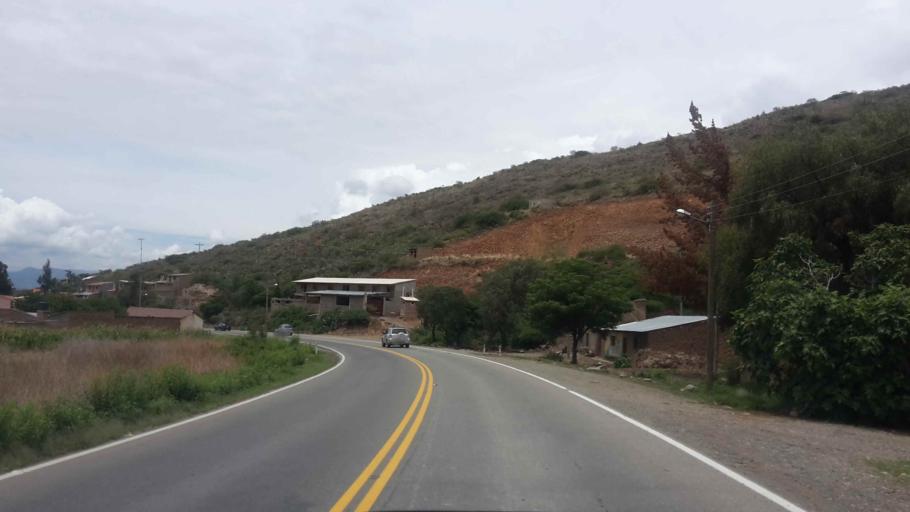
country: BO
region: Cochabamba
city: Punata
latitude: -17.5141
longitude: -65.8150
